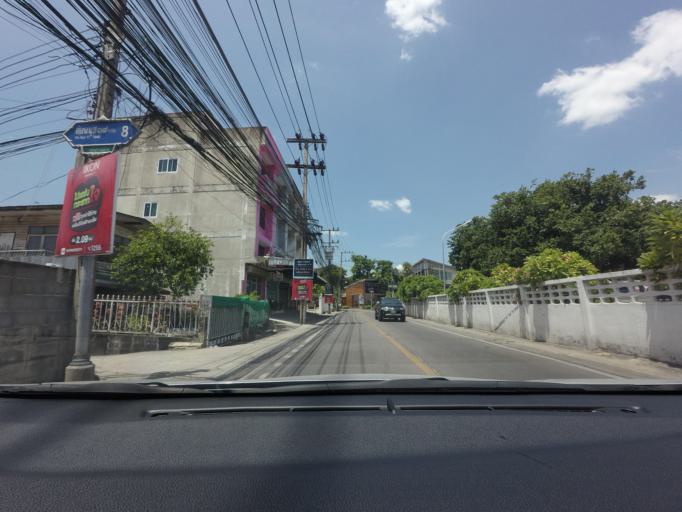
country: TH
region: Bangkok
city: Phra Khanong
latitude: 13.7137
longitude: 100.6106
